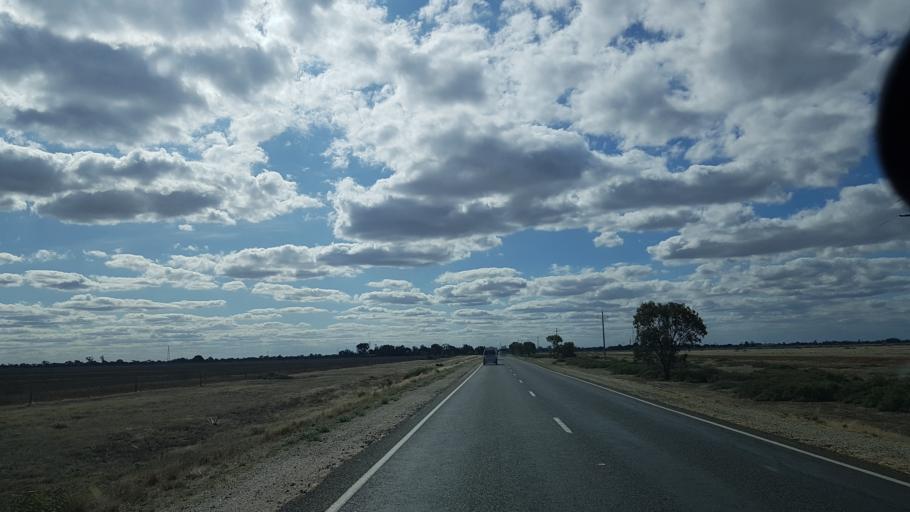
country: AU
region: Victoria
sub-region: Swan Hill
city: Swan Hill
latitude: -35.7886
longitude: 143.9439
